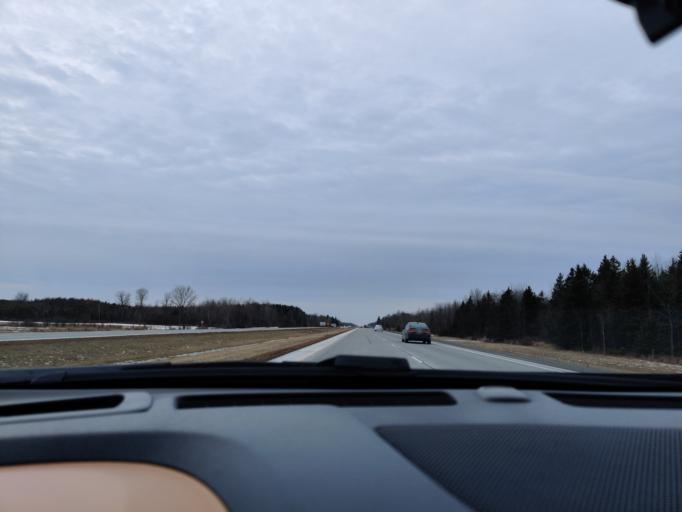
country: US
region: New York
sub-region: St. Lawrence County
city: Ogdensburg
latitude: 44.8305
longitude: -75.3740
